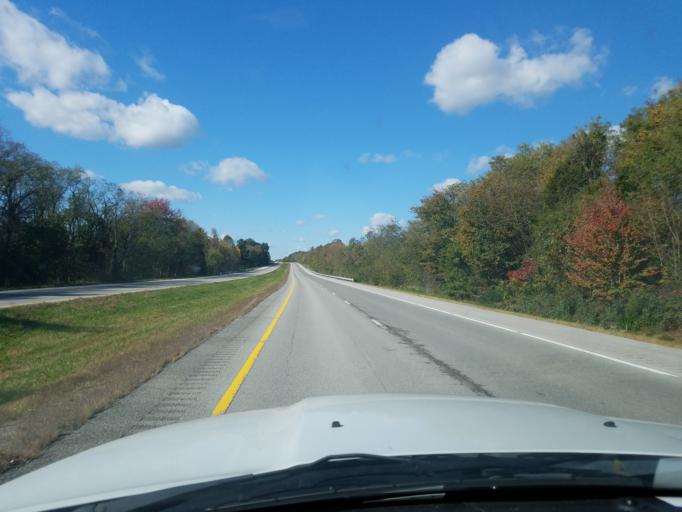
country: US
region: Kentucky
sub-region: Metcalfe County
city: Edmonton
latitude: 36.9985
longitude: -85.7262
